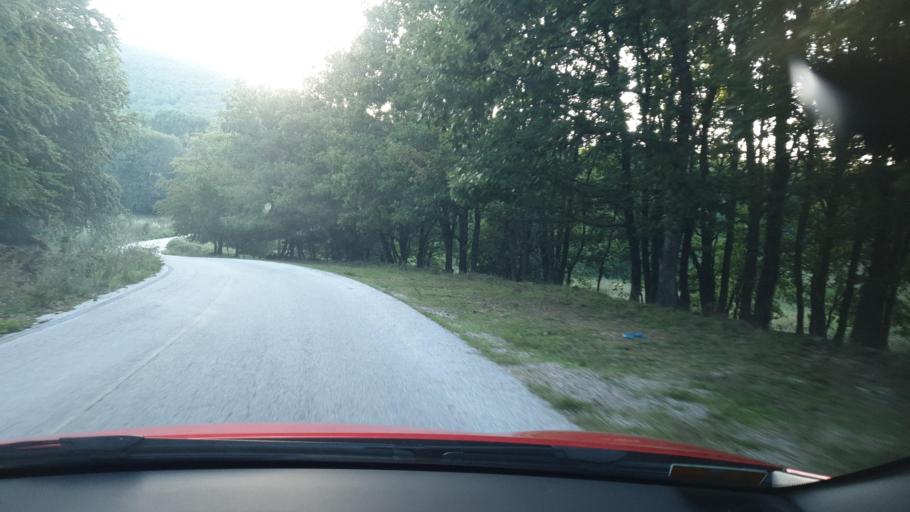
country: GR
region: Central Macedonia
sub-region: Nomos Chalkidikis
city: Galatista
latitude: 40.5039
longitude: 23.2295
